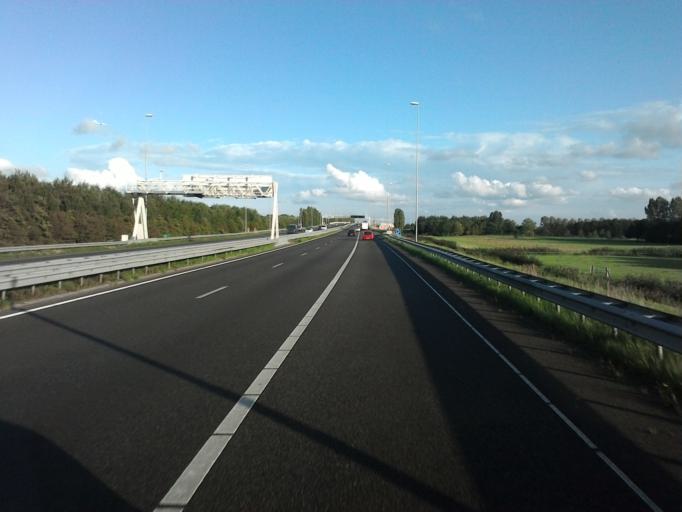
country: NL
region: North Holland
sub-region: Gemeente Velsen
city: Velsen-Zuid
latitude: 52.4242
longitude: 4.6861
